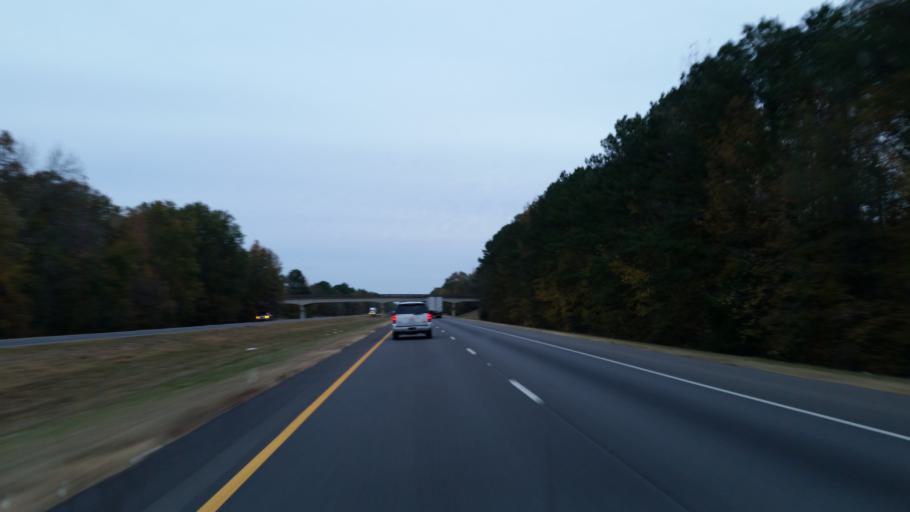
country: US
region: Alabama
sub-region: Greene County
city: Eutaw
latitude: 32.7585
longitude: -88.0735
